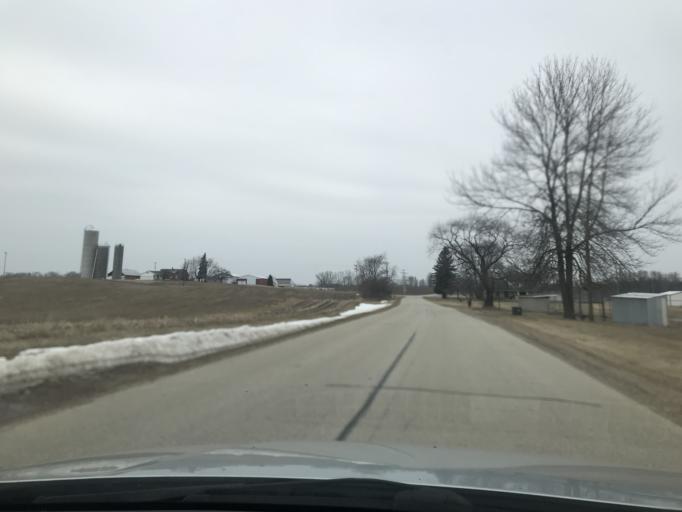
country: US
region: Wisconsin
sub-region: Marinette County
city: Peshtigo
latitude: 45.0325
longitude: -87.8670
